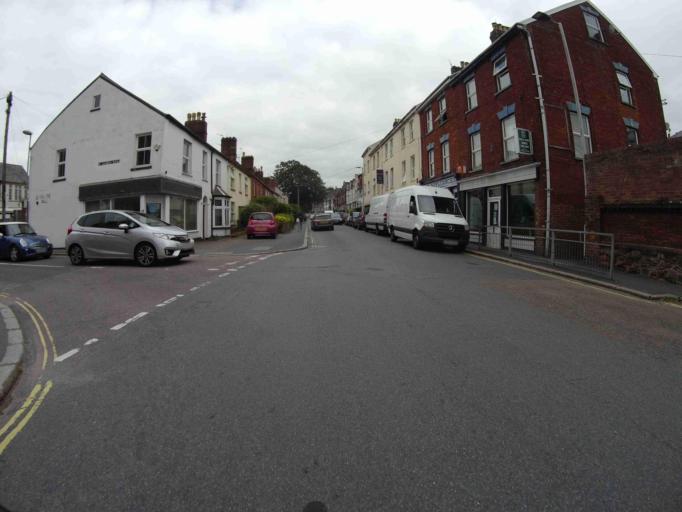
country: GB
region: England
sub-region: Devon
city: Exeter
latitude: 50.7295
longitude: -3.5203
